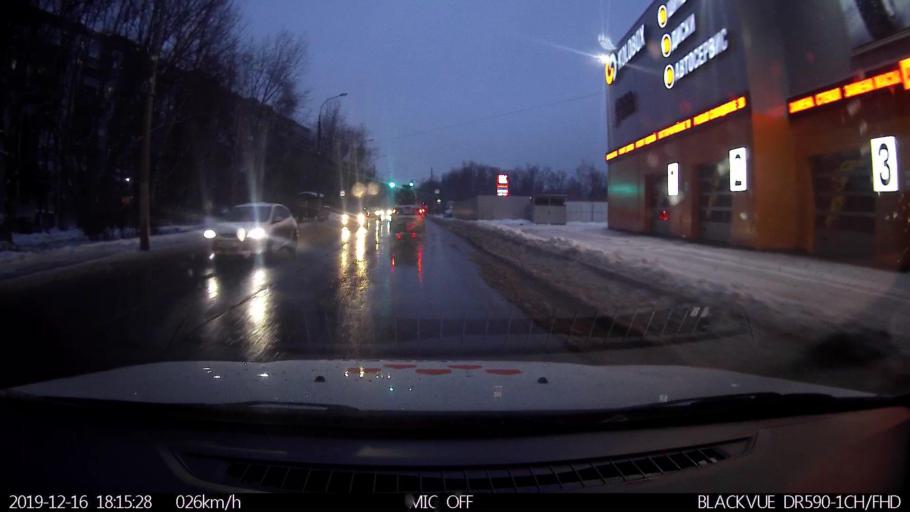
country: RU
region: Nizjnij Novgorod
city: Nizhniy Novgorod
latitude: 56.2870
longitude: 43.9533
